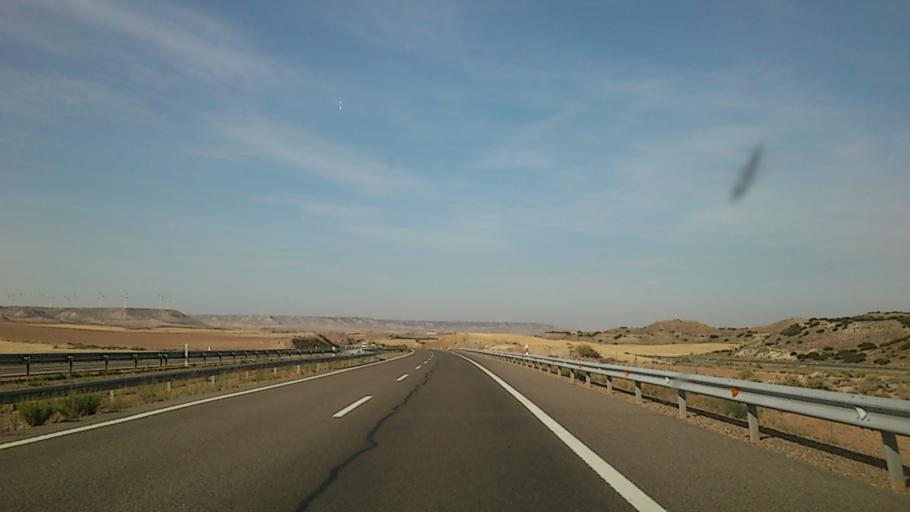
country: ES
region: Aragon
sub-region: Provincia de Zaragoza
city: Longares
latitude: 41.4287
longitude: -1.1472
